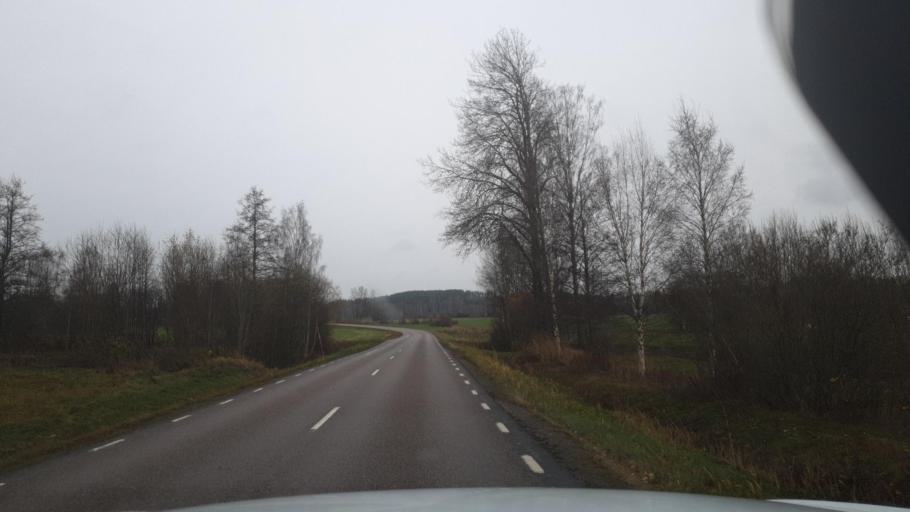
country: SE
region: Vaermland
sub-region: Arvika Kommun
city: Arvika
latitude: 59.4947
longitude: 12.6847
